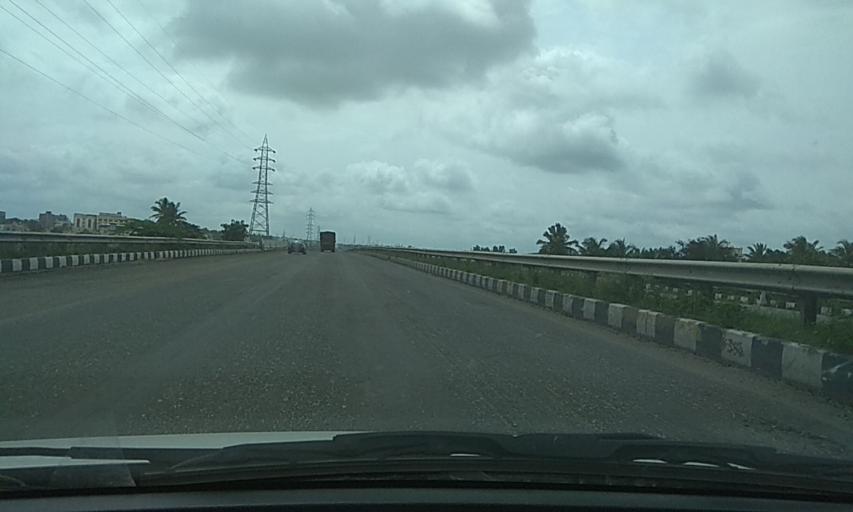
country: IN
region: Karnataka
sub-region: Davanagere
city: Harihar
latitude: 14.4416
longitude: 75.8985
